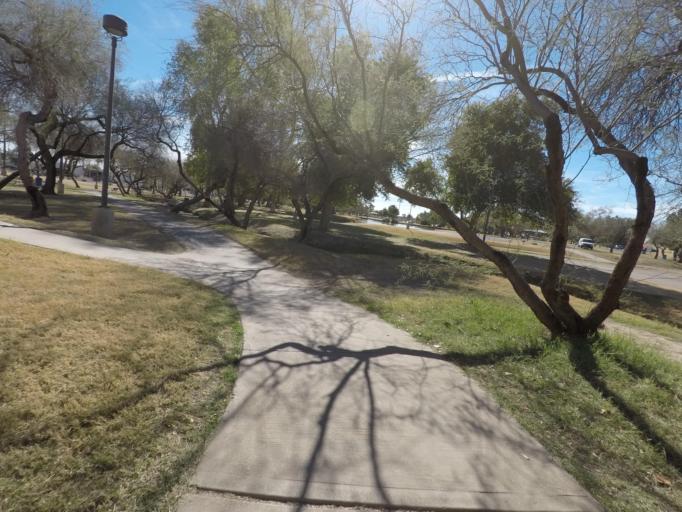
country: US
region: Arizona
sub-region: Maricopa County
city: Scottsdale
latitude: 33.4700
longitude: -111.9154
